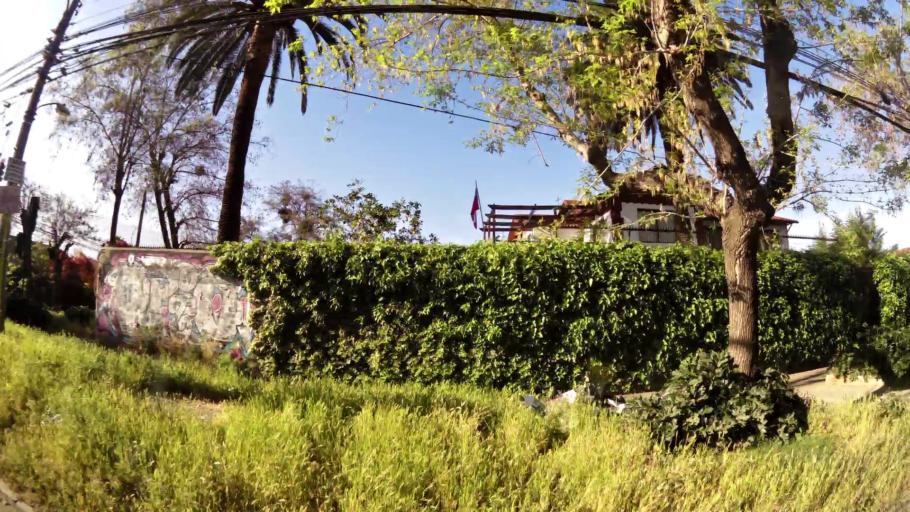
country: CL
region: Santiago Metropolitan
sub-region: Provincia de Santiago
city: Villa Presidente Frei, Nunoa, Santiago, Chile
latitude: -33.4554
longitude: -70.5668
